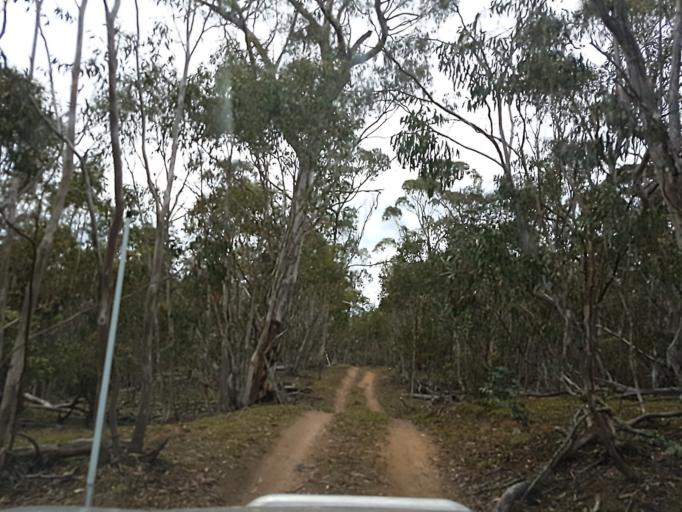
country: AU
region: New South Wales
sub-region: Snowy River
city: Jindabyne
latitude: -36.8514
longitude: 148.2566
